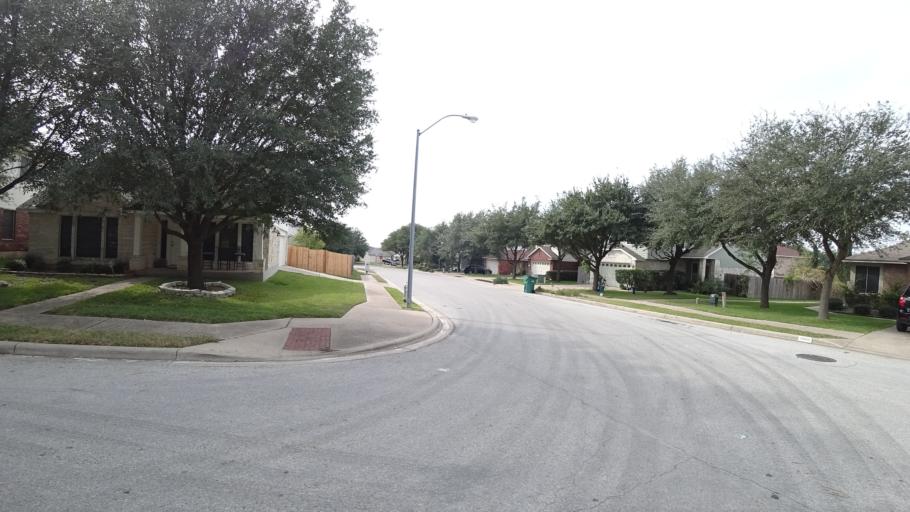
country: US
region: Texas
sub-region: Travis County
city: Windemere
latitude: 30.4441
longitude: -97.6553
